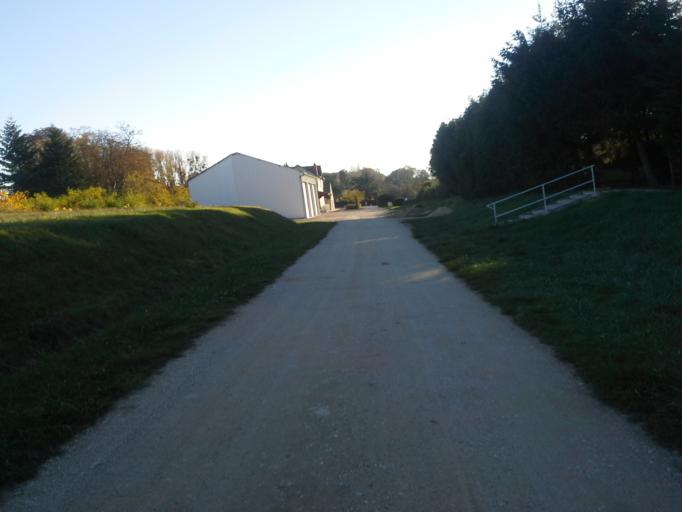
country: FR
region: Centre
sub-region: Departement du Loir-et-Cher
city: Saint-Romain-sur-Cher
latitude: 47.3653
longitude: 1.4011
